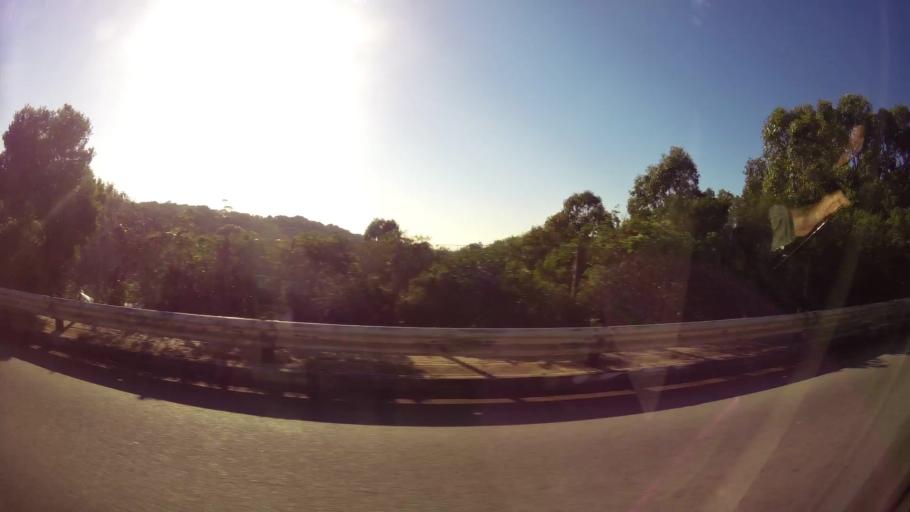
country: ZA
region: Eastern Cape
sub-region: Nelson Mandela Bay Metropolitan Municipality
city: Port Elizabeth
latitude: -33.9774
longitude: 25.6266
